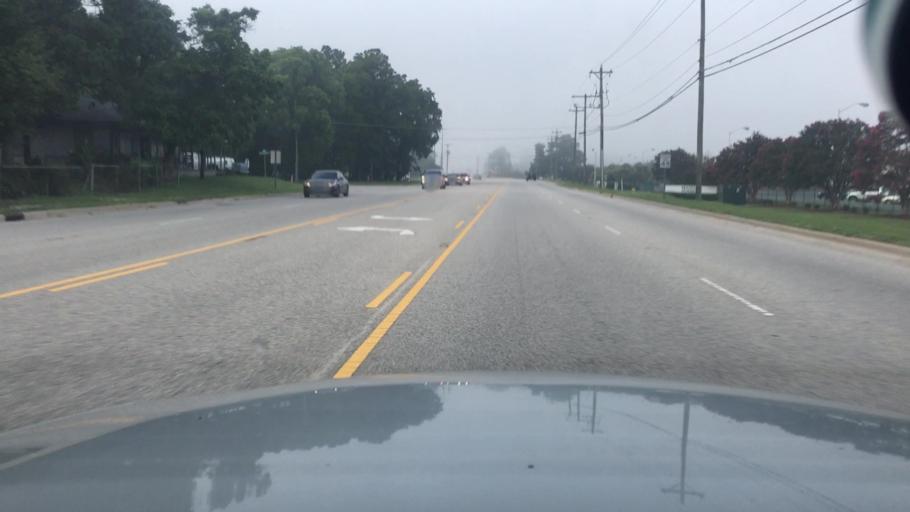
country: US
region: North Carolina
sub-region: Cumberland County
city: Hope Mills
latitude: 35.0142
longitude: -78.9189
